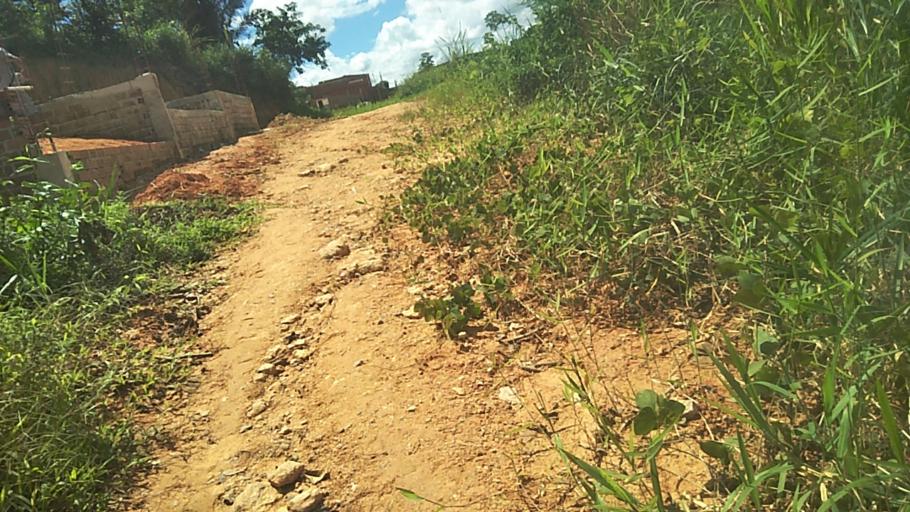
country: BR
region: Pernambuco
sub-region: Jaboatao Dos Guararapes
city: Jaboatao dos Guararapes
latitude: -8.0692
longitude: -35.0053
